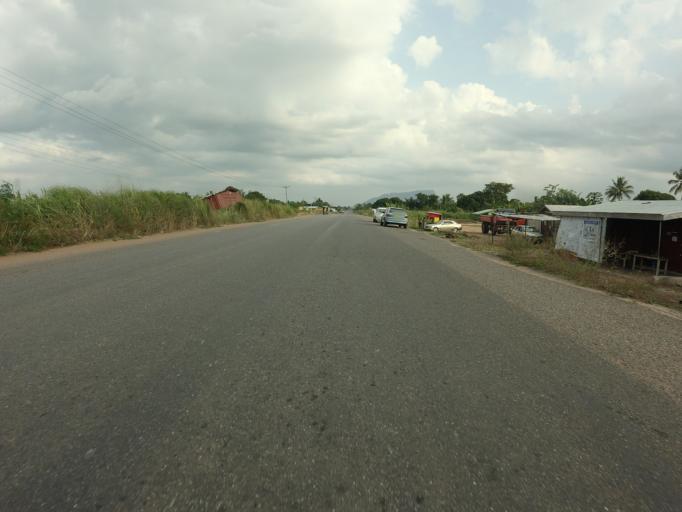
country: GH
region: Volta
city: Ho
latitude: 6.5794
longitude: 0.4822
